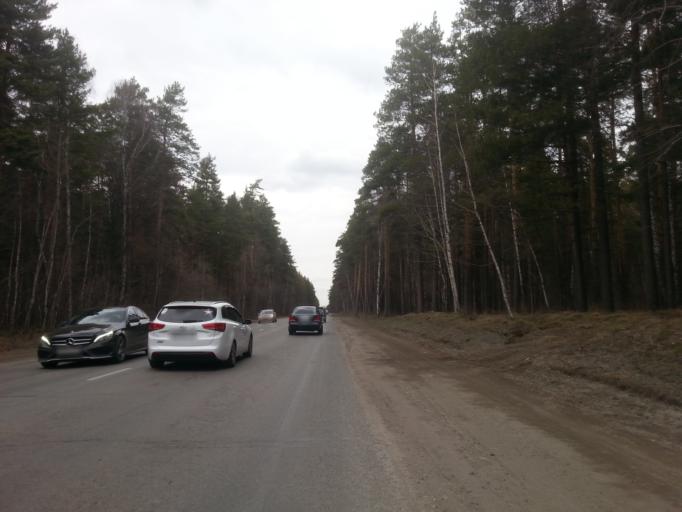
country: RU
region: Altai Krai
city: Yuzhnyy
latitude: 53.2789
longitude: 83.7182
